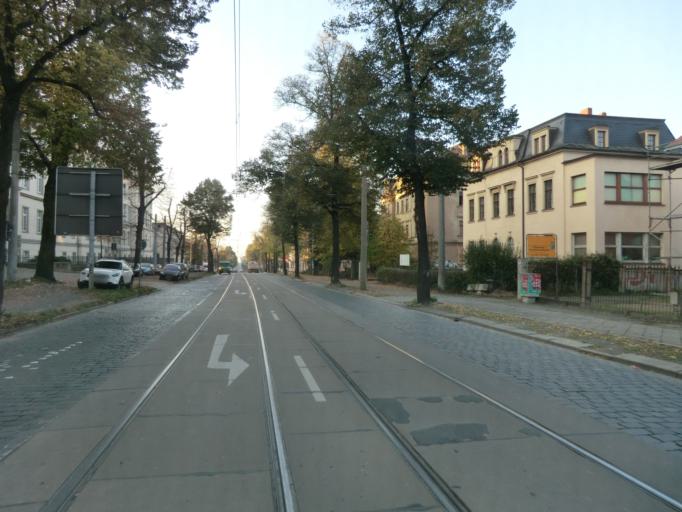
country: DE
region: Saxony
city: Albertstadt
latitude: 51.0761
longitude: 13.7549
